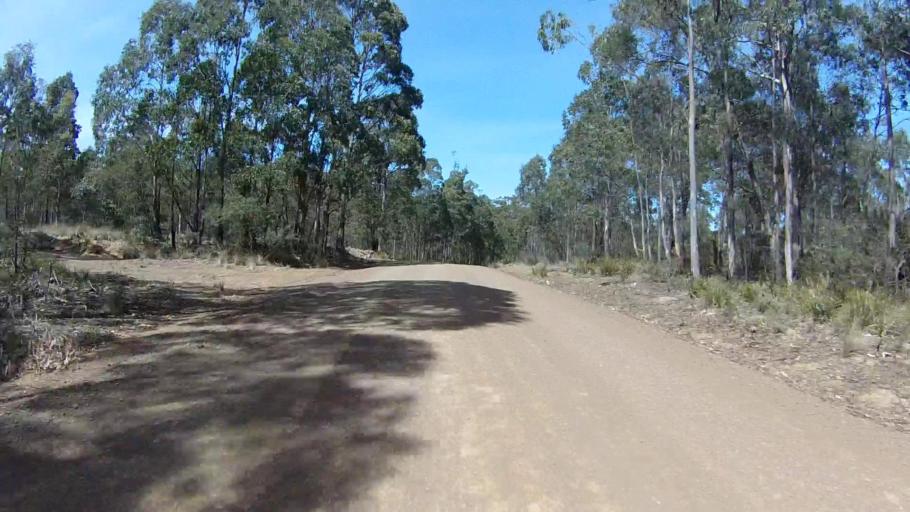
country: AU
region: Tasmania
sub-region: Sorell
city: Sorell
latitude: -42.6690
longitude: 147.7301
